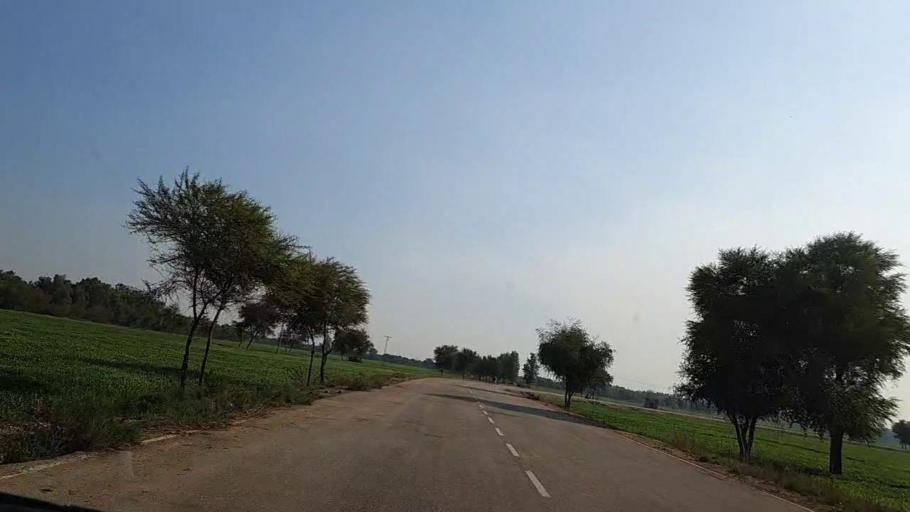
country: PK
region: Sindh
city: Sakrand
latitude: 26.1192
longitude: 68.2494
